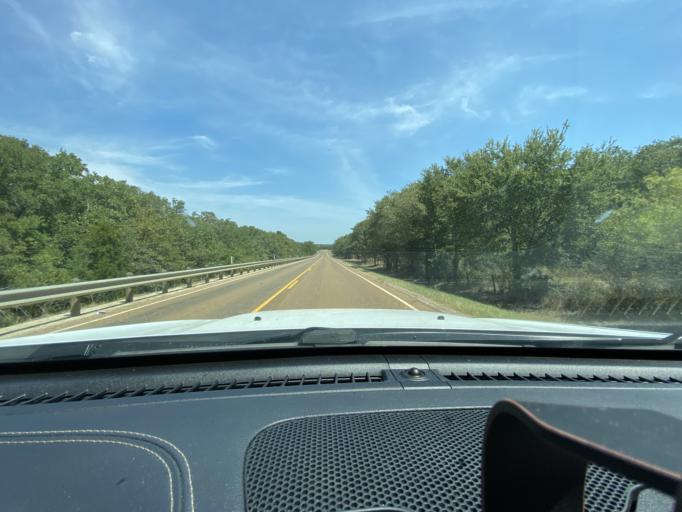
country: US
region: Texas
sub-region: Bastrop County
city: Smithville
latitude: 30.1336
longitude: -97.0805
